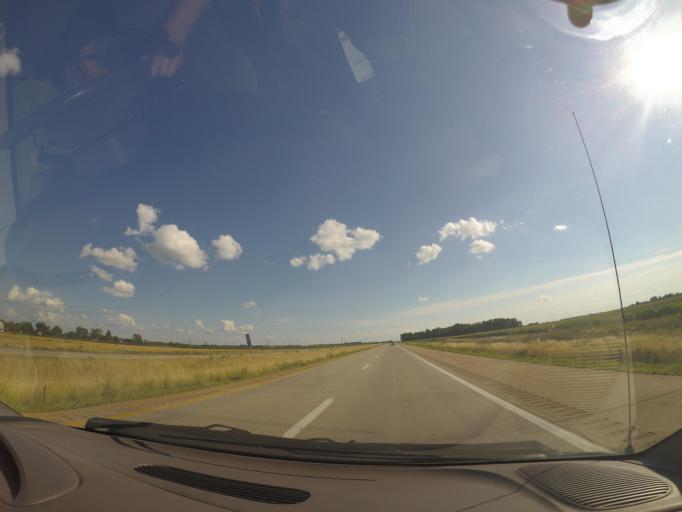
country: US
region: Ohio
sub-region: Lucas County
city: Whitehouse
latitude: 41.4884
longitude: -83.7708
